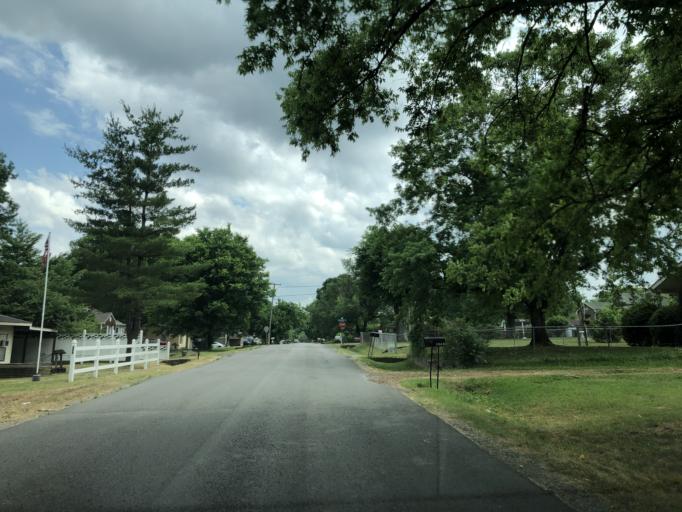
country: US
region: Tennessee
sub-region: Davidson County
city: Goodlettsville
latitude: 36.2702
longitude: -86.6909
